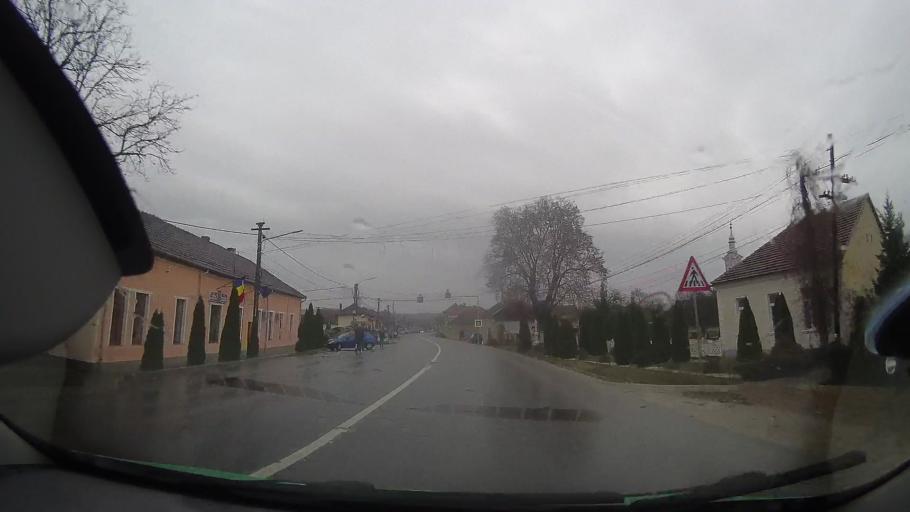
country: RO
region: Bihor
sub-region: Comuna Pocola
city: Pocola
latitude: 46.6948
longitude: 22.2932
